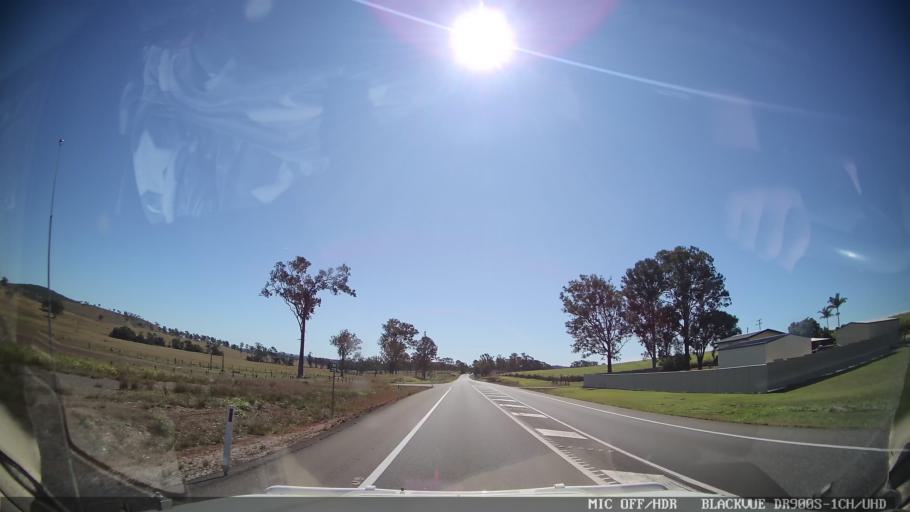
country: AU
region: Queensland
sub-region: Fraser Coast
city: Maryborough
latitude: -25.7798
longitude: 152.5964
